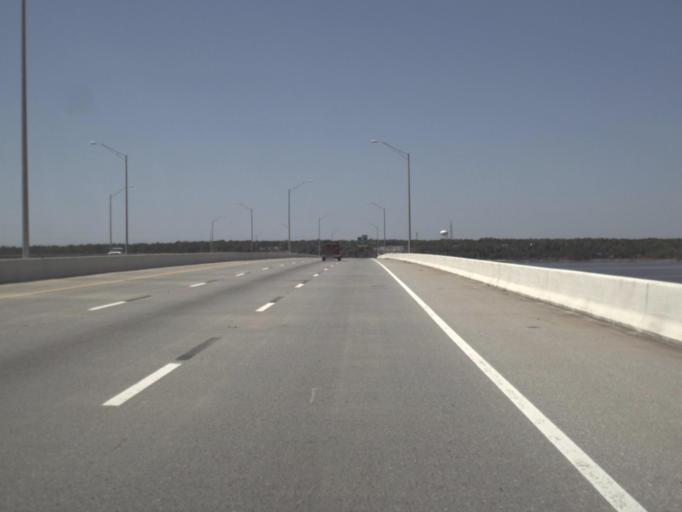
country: US
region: Florida
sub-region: Escambia County
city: Ferry Pass
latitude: 30.5171
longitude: -87.1472
